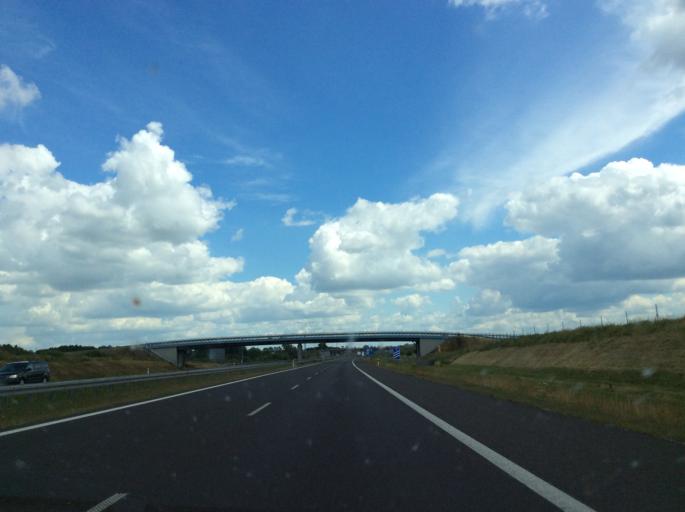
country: PL
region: Greater Poland Voivodeship
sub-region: Powiat kolski
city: Koscielec
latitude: 52.1417
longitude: 18.5957
